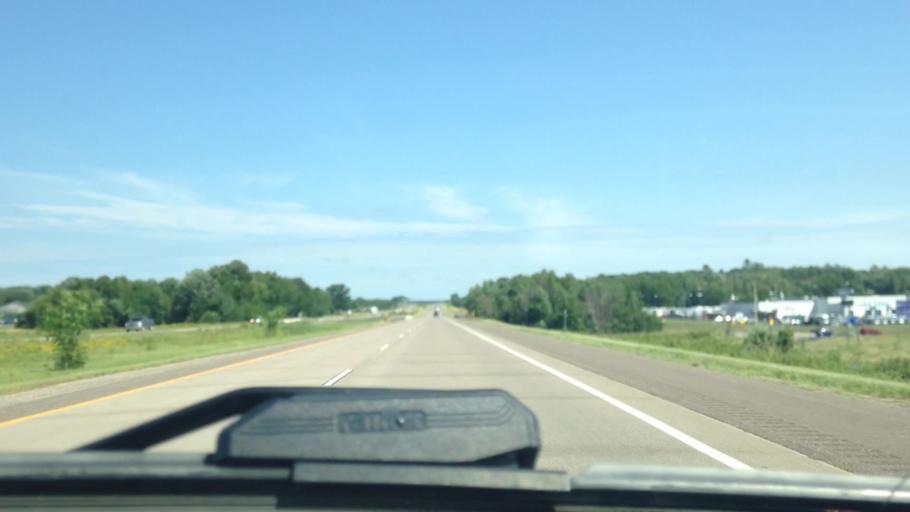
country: US
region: Wisconsin
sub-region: Barron County
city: Rice Lake
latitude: 45.4709
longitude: -91.7582
